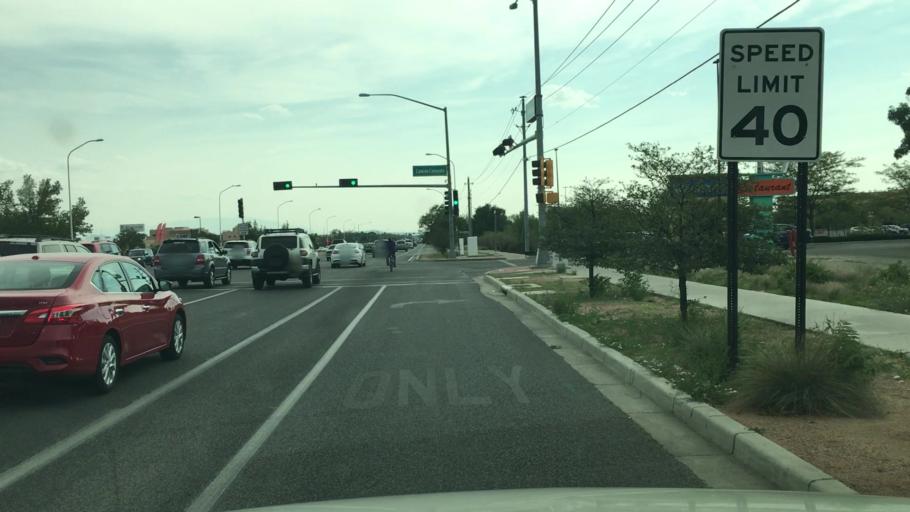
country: US
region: New Mexico
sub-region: Santa Fe County
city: Agua Fria
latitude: 35.6524
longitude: -105.9968
